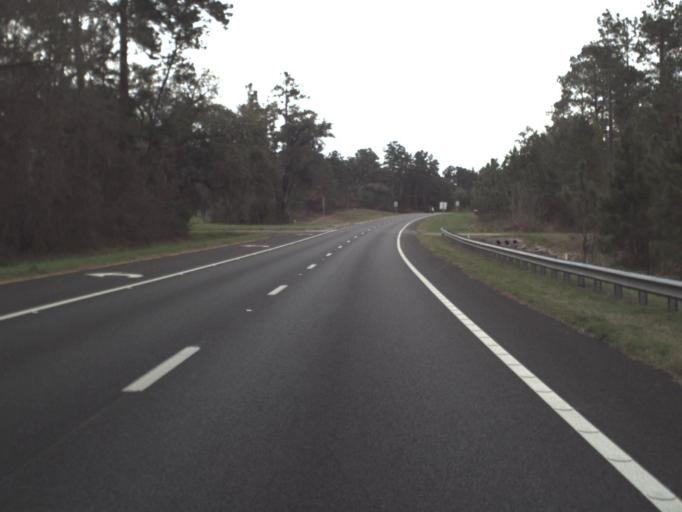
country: US
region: Georgia
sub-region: Grady County
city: Cairo
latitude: 30.6612
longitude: -84.1680
